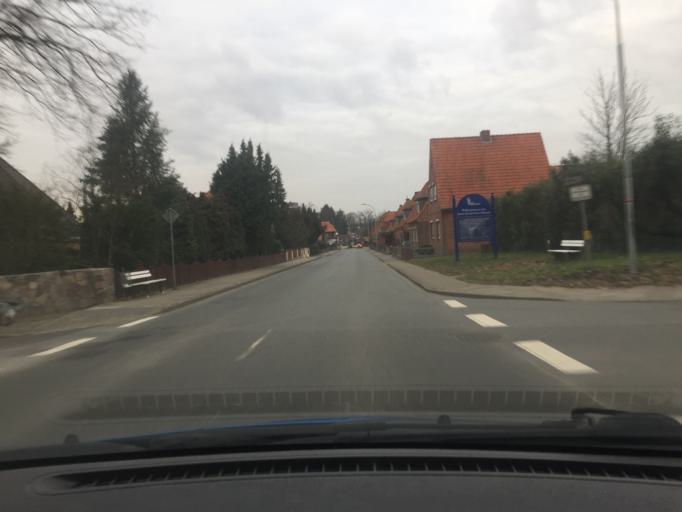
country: DE
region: Lower Saxony
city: Bad Bevensen
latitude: 53.0772
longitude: 10.5922
